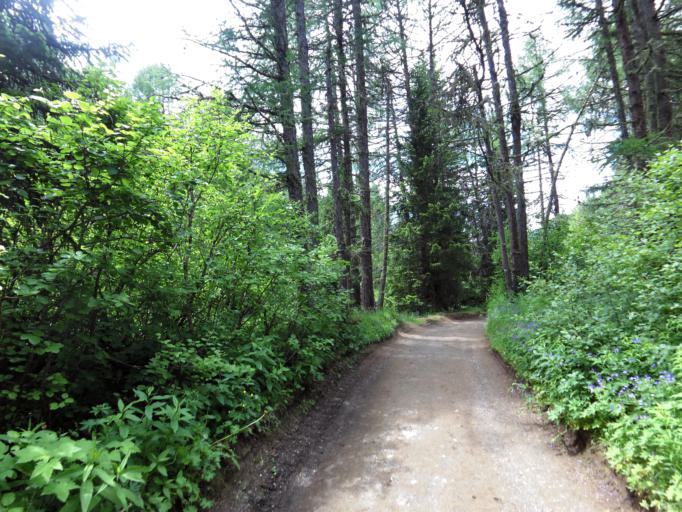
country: IT
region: Trentino-Alto Adige
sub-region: Bolzano
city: Ortisei
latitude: 46.5393
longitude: 11.6384
